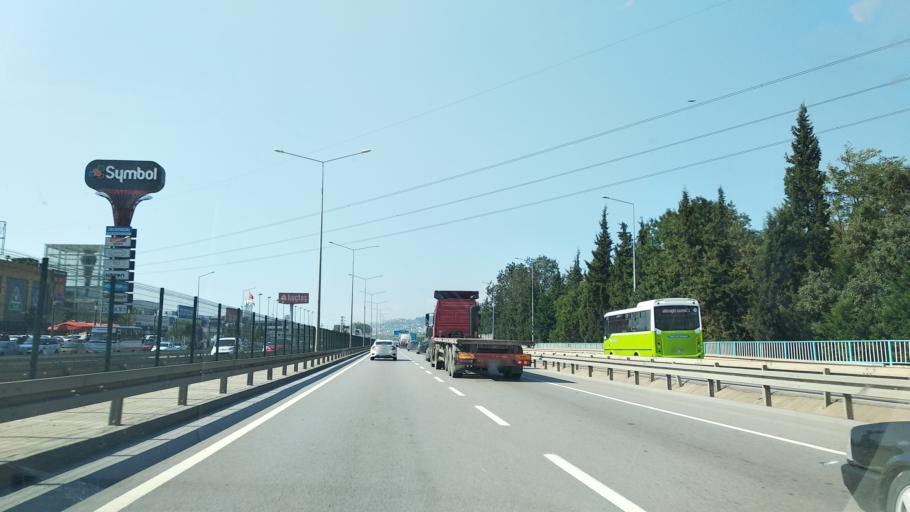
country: TR
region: Kocaeli
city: Kullar
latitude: 40.7595
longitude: 29.9813
